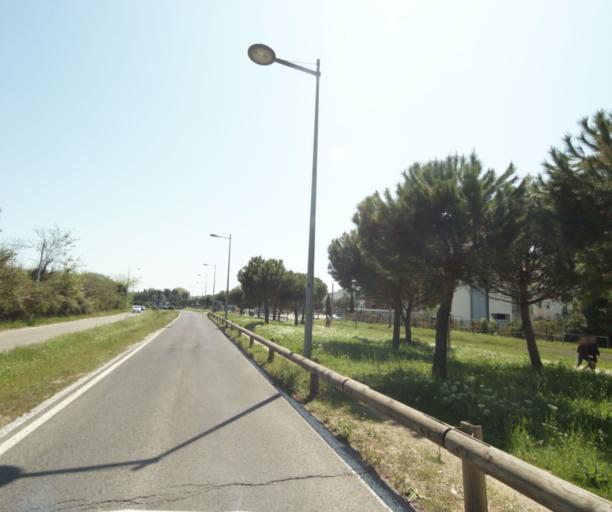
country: FR
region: Languedoc-Roussillon
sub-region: Departement de l'Herault
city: Juvignac
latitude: 43.6355
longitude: 3.8325
